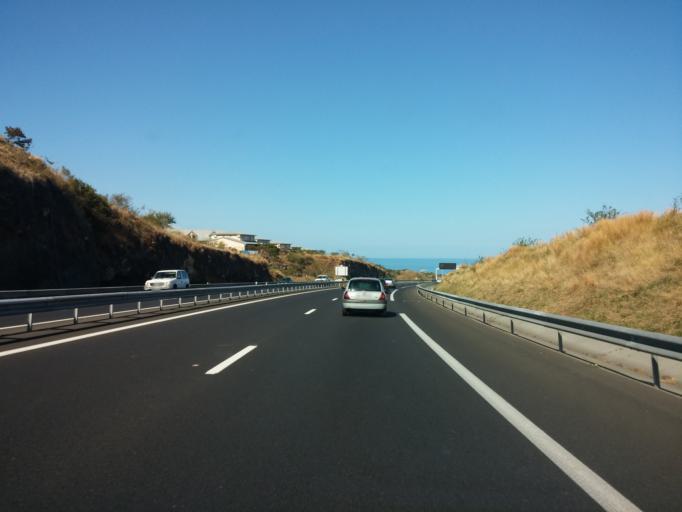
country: RE
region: Reunion
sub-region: Reunion
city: Saint-Leu
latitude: -21.1966
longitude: 55.2958
